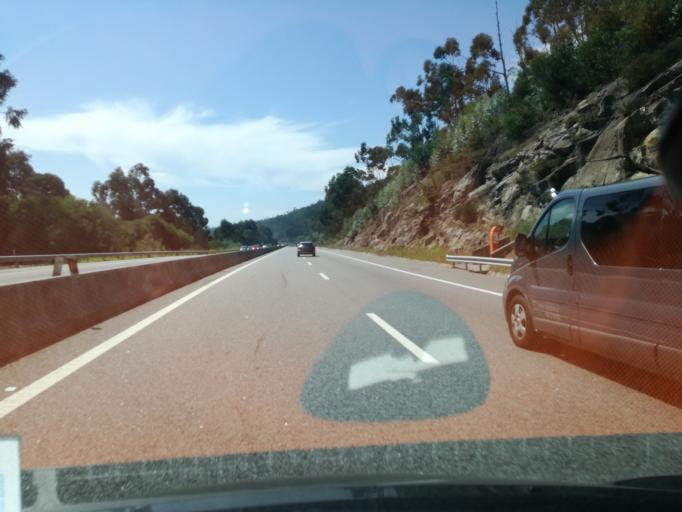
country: PT
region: Viana do Castelo
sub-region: Viana do Castelo
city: Meadela
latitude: 41.7568
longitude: -8.7958
